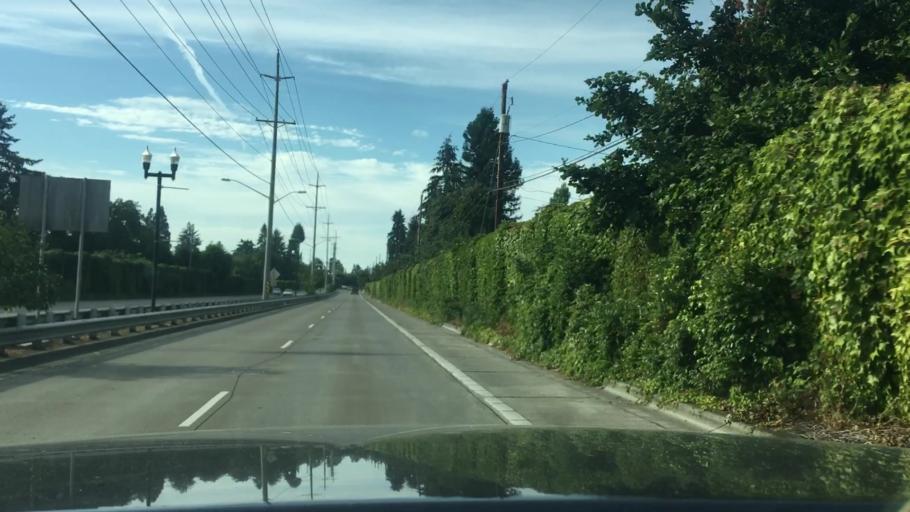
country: US
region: Oregon
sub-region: Lane County
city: Springfield
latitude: 44.0729
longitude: -123.0296
